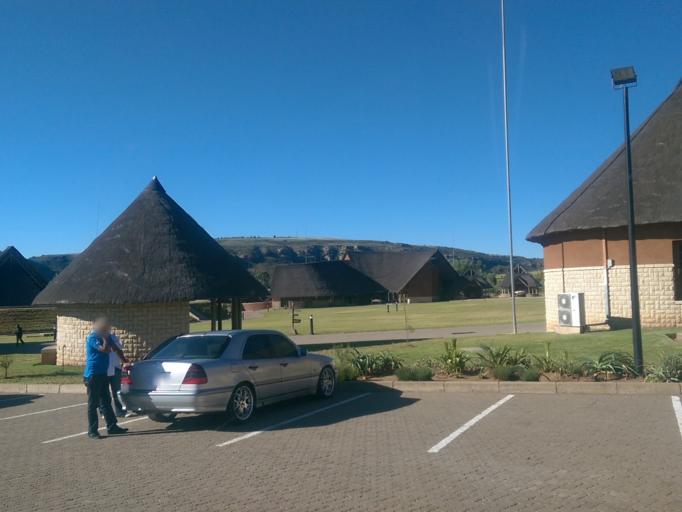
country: LS
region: Maseru
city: Maseru
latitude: -29.3464
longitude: 27.6618
